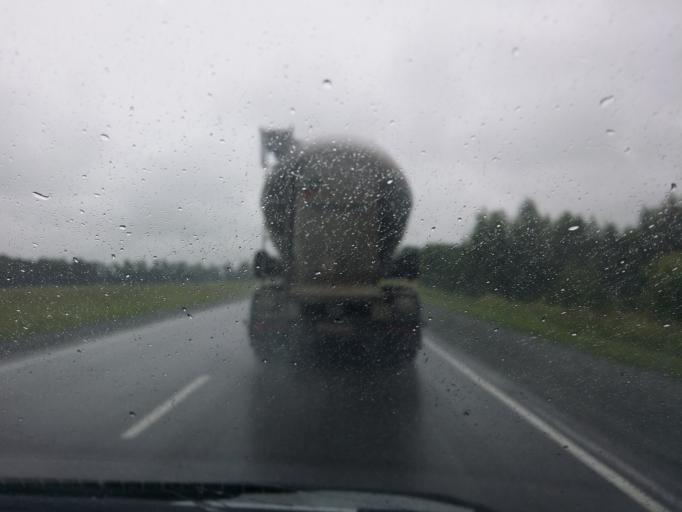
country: RU
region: Altai Krai
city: Bayunovskiye Klyuchi
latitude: 53.3031
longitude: 84.2628
